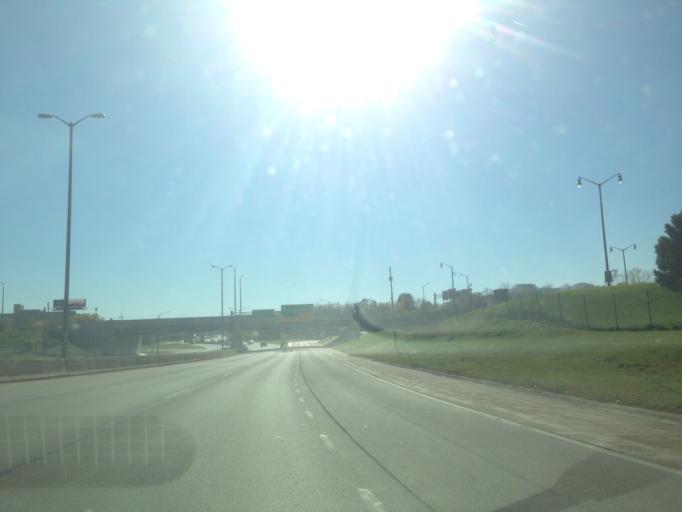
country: US
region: Wisconsin
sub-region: Milwaukee County
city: West Milwaukee
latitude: 43.0280
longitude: -87.9693
